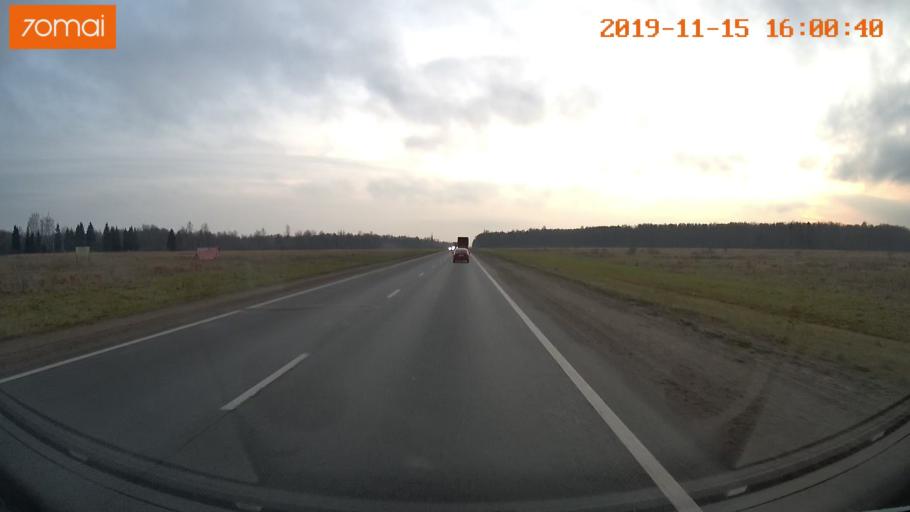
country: RU
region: Jaroslavl
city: Yaroslavl
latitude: 57.7932
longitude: 39.9372
